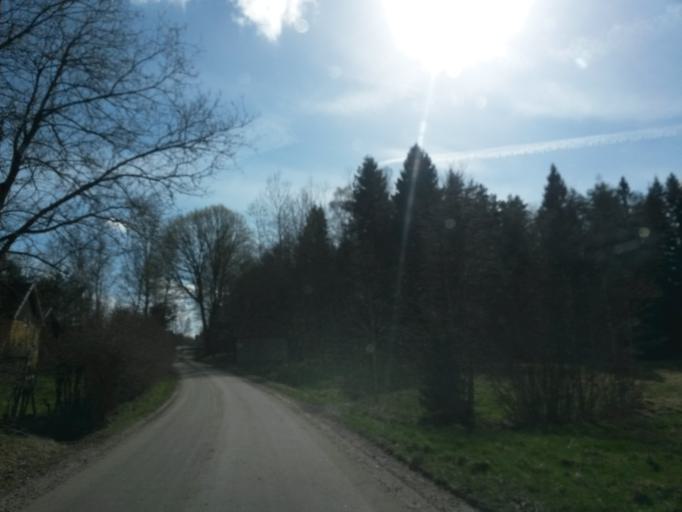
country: SE
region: Vaestra Goetaland
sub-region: Vargarda Kommun
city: Jonstorp
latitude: 57.9747
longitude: 12.7415
